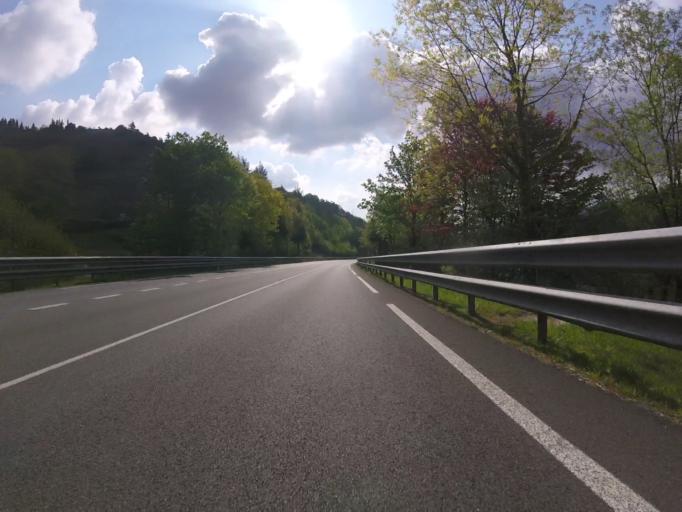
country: ES
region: Basque Country
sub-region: Provincia de Guipuzcoa
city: Azkoitia
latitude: 43.1981
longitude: -2.3404
